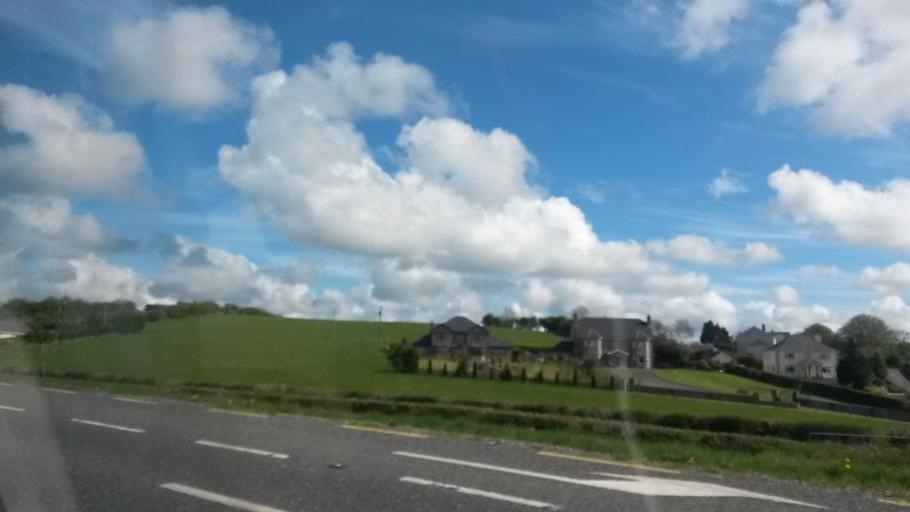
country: IE
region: Ulster
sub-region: An Cabhan
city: Virginia
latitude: 53.8566
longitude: -7.1054
